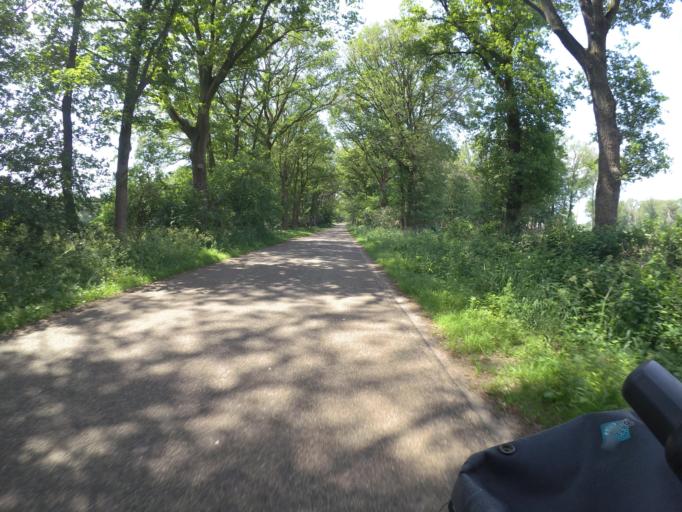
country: NL
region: Overijssel
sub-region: Gemeente Hof van Twente
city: Markelo
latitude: 52.2750
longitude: 6.4663
